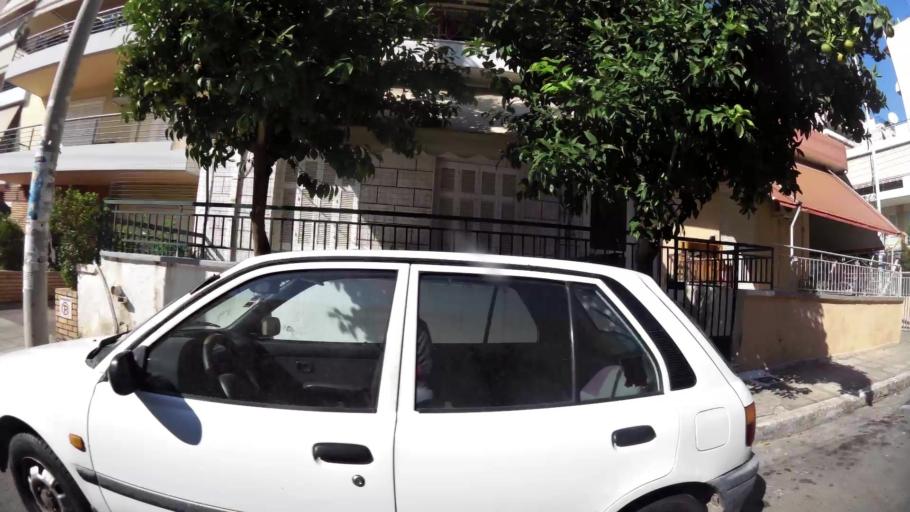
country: GR
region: Attica
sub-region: Nomos Piraios
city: Keratsini
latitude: 37.9648
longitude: 23.6210
